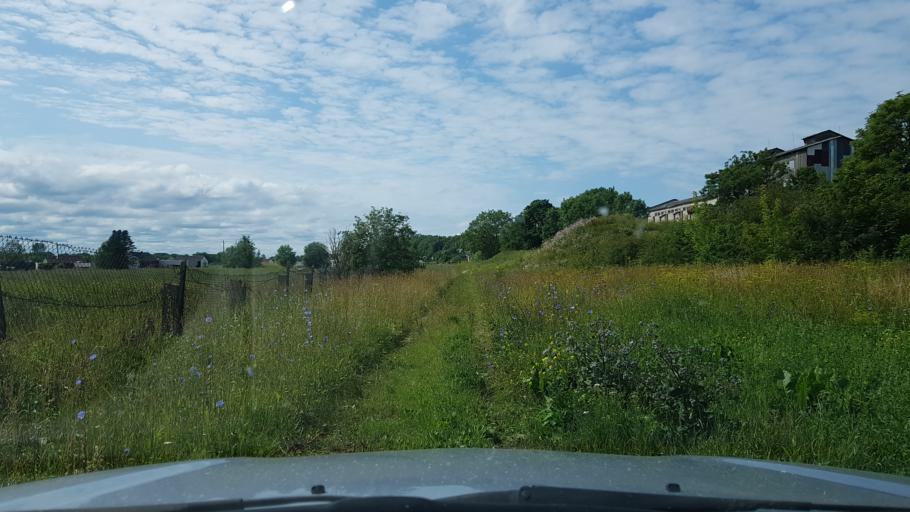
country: EE
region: Ida-Virumaa
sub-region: Sillamaee linn
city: Sillamae
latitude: 59.3714
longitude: 27.8771
